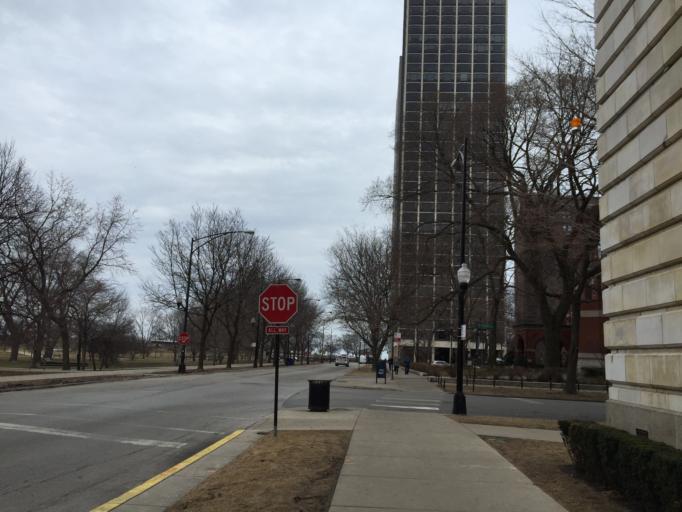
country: US
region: Illinois
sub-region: Cook County
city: Chicago
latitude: 41.9112
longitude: -87.6292
